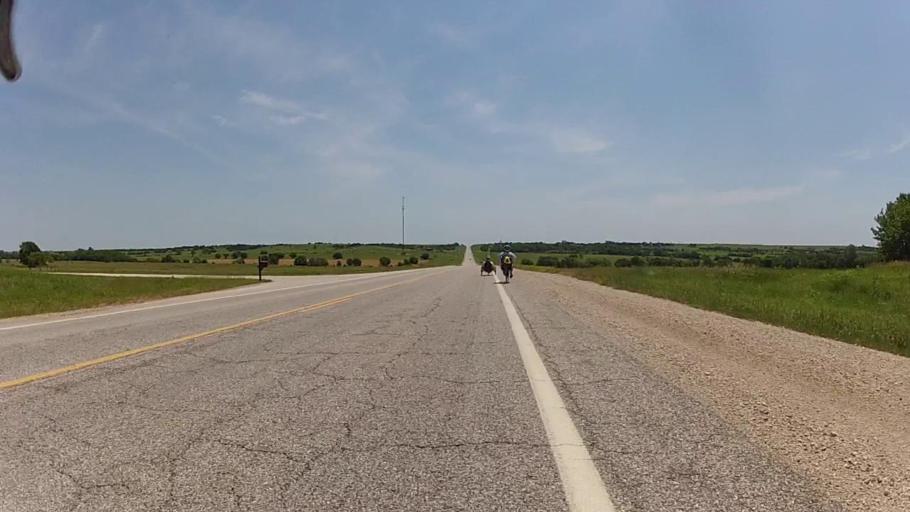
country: US
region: Kansas
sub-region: Chautauqua County
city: Sedan
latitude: 37.1133
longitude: -96.4628
